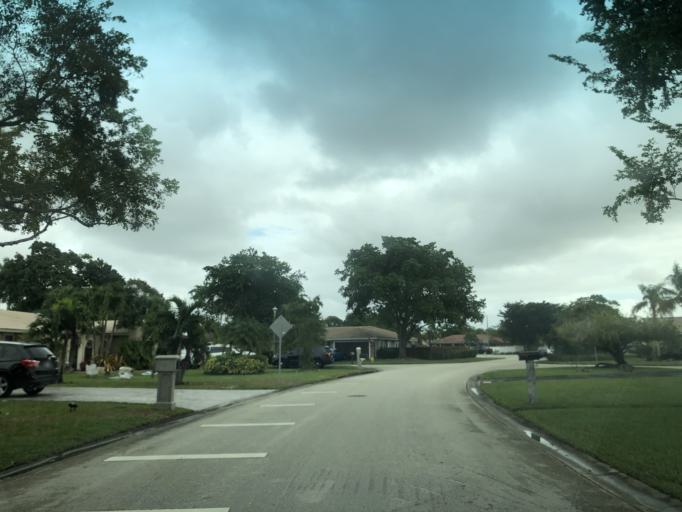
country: US
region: Florida
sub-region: Broward County
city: Margate
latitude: 26.2548
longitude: -80.2393
